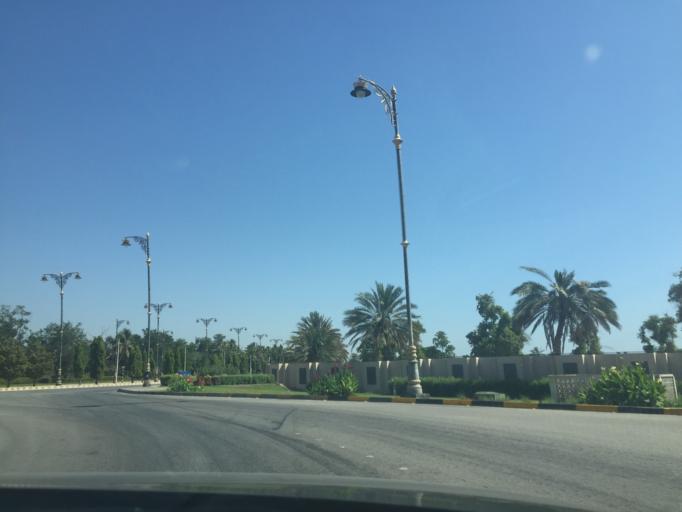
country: OM
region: Zufar
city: Salalah
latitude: 17.0259
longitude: 54.1435
